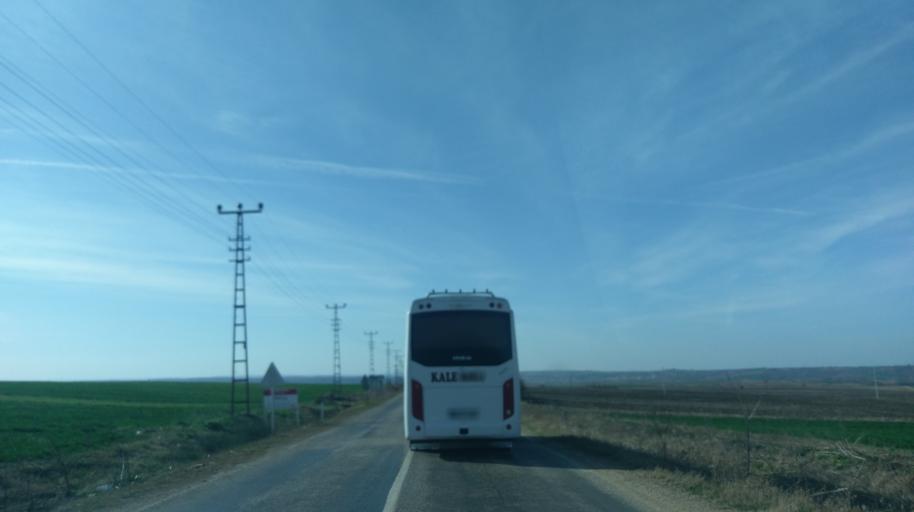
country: TR
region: Edirne
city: Copkoy
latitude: 41.3056
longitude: 26.8163
